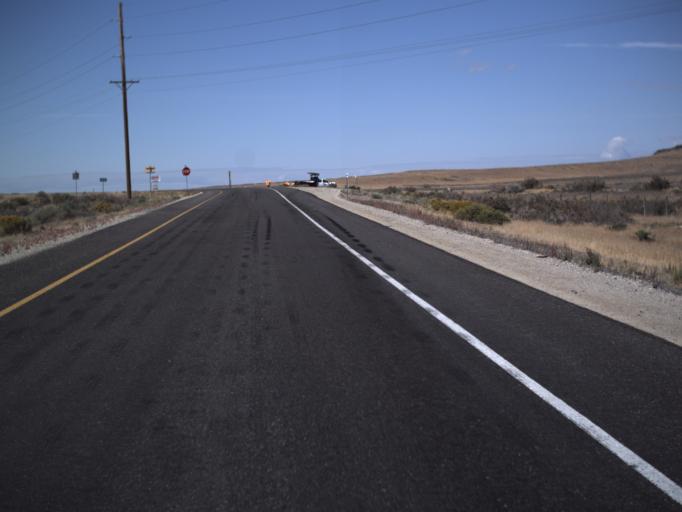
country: US
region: Utah
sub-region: Tooele County
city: Grantsville
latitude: 40.7336
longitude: -113.1126
